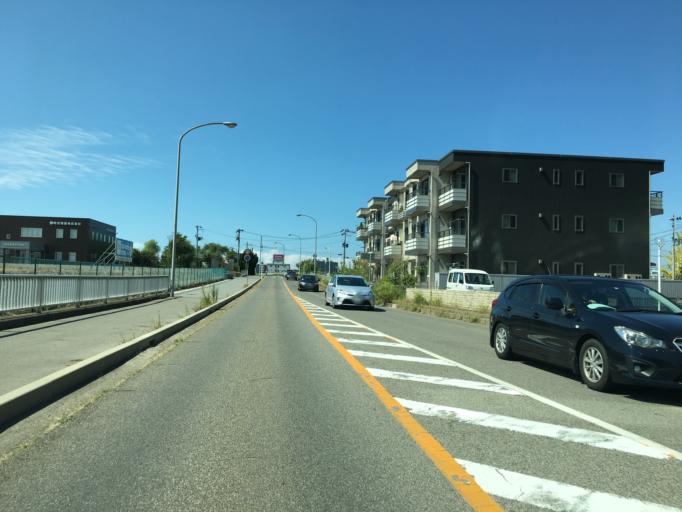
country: JP
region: Niigata
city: Niigata-shi
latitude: 37.8965
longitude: 139.0173
